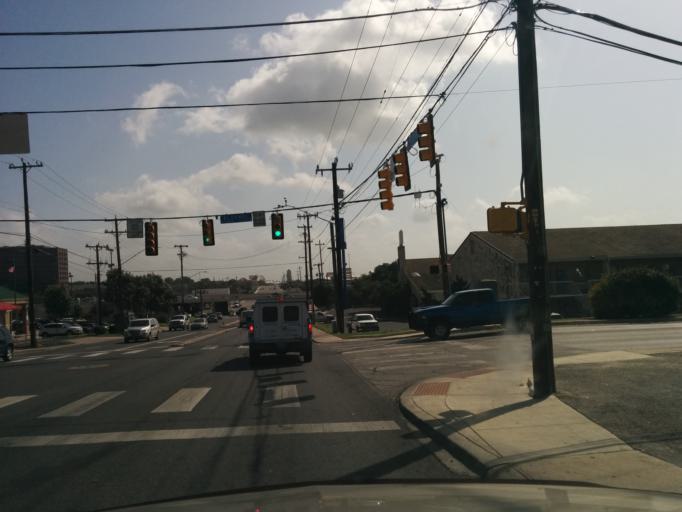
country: US
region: Texas
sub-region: Bexar County
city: Balcones Heights
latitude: 29.5294
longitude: -98.5638
